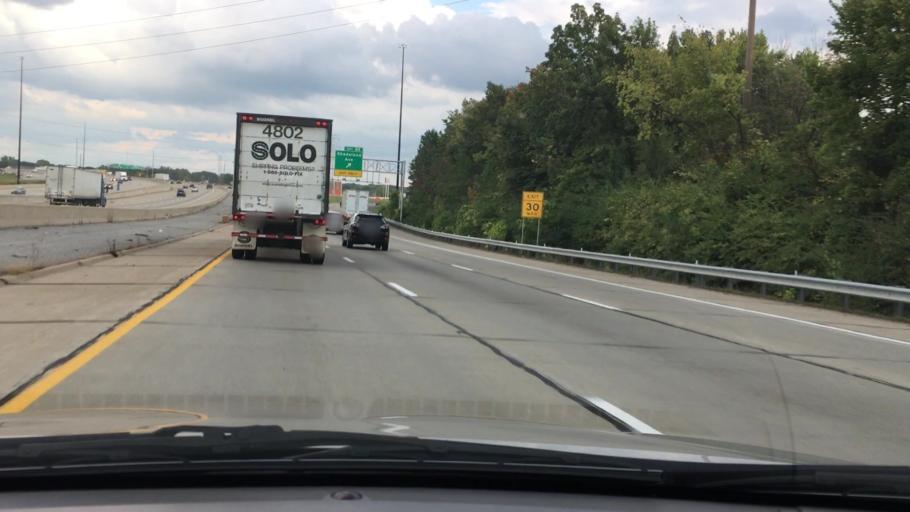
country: US
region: Indiana
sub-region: Marion County
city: Warren Park
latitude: 39.8022
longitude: -86.0518
